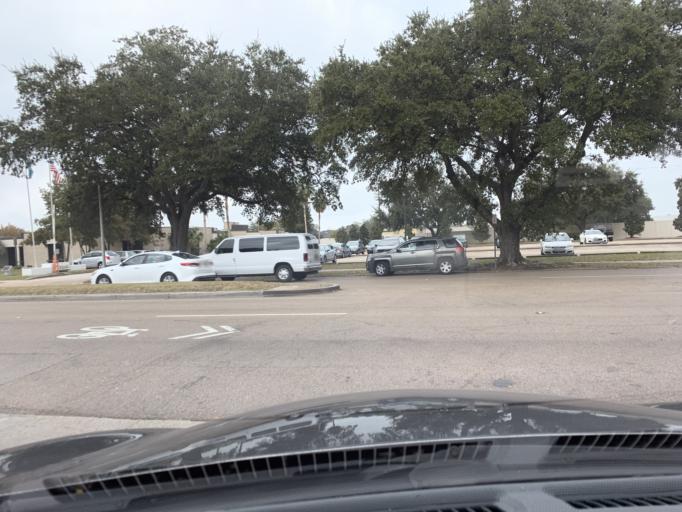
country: US
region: Louisiana
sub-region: Orleans Parish
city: New Orleans
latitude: 29.9835
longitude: -90.1053
